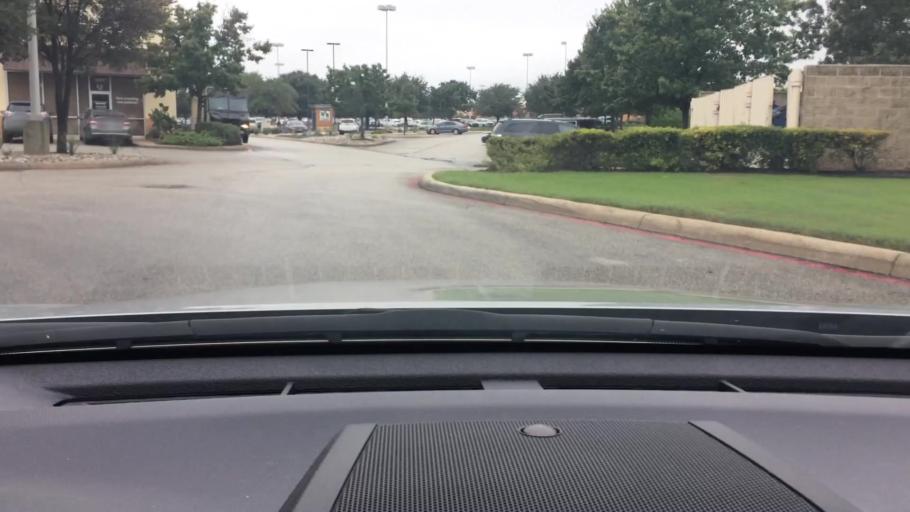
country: US
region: Texas
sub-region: Bexar County
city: Helotes
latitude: 29.4942
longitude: -98.7074
